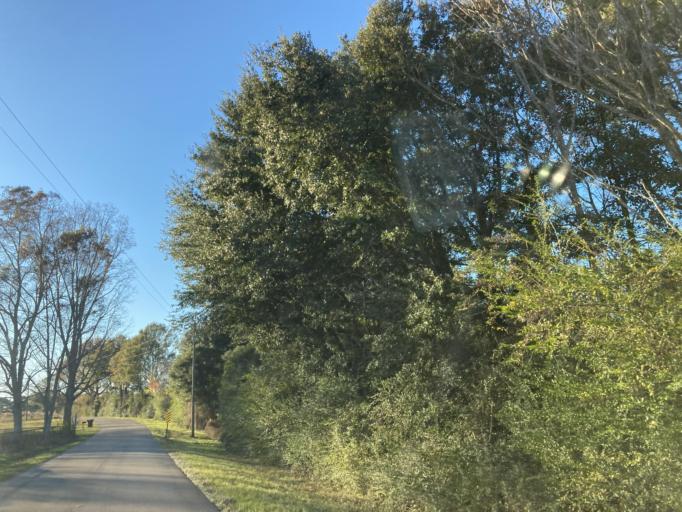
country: US
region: Mississippi
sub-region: Lamar County
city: Sumrall
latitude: 31.2680
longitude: -89.5977
